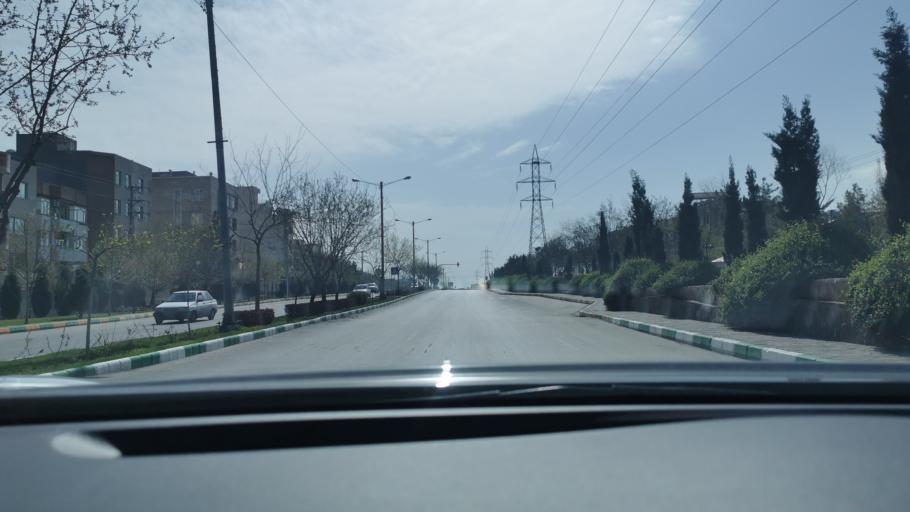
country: IR
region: Razavi Khorasan
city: Mashhad
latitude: 36.2892
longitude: 59.5324
